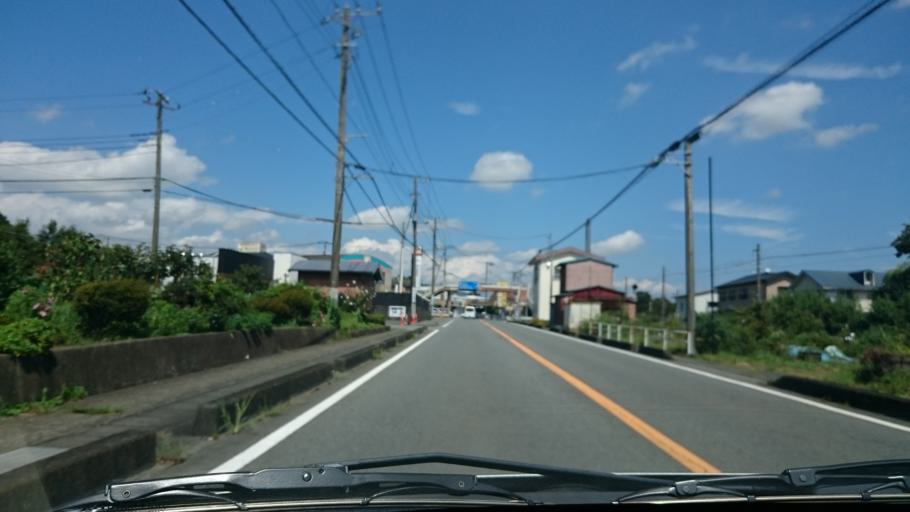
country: JP
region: Shizuoka
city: Gotemba
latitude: 35.2747
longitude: 138.9242
